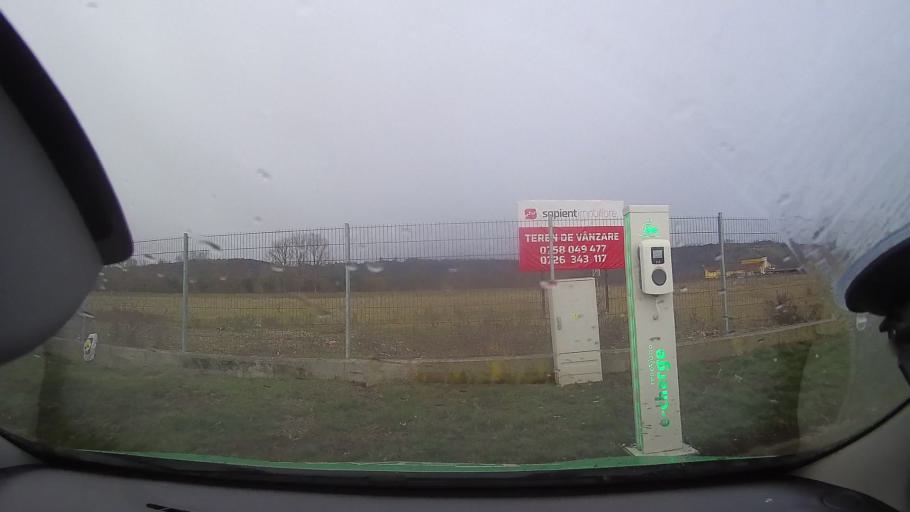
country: RO
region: Cluj
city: Turda
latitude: 46.5608
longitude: 23.8172
